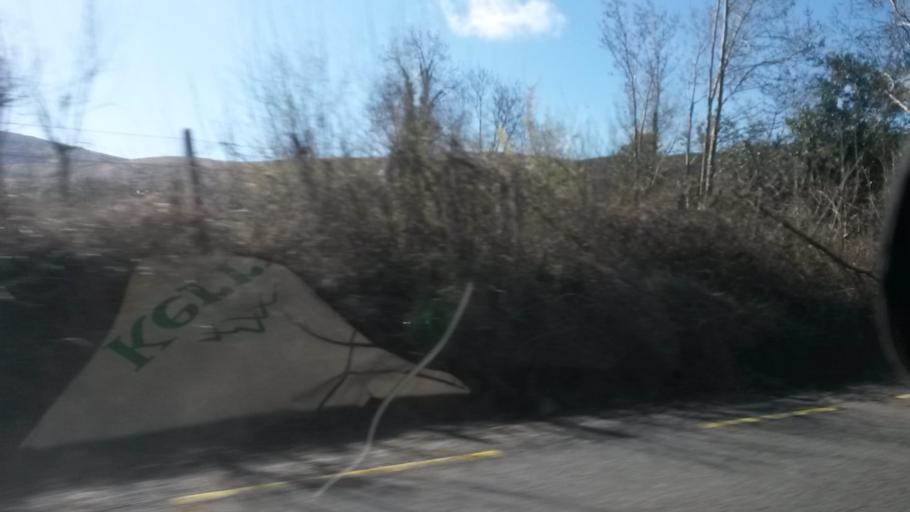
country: IE
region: Munster
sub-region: Ciarrai
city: Kenmare
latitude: 51.9091
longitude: -9.4108
